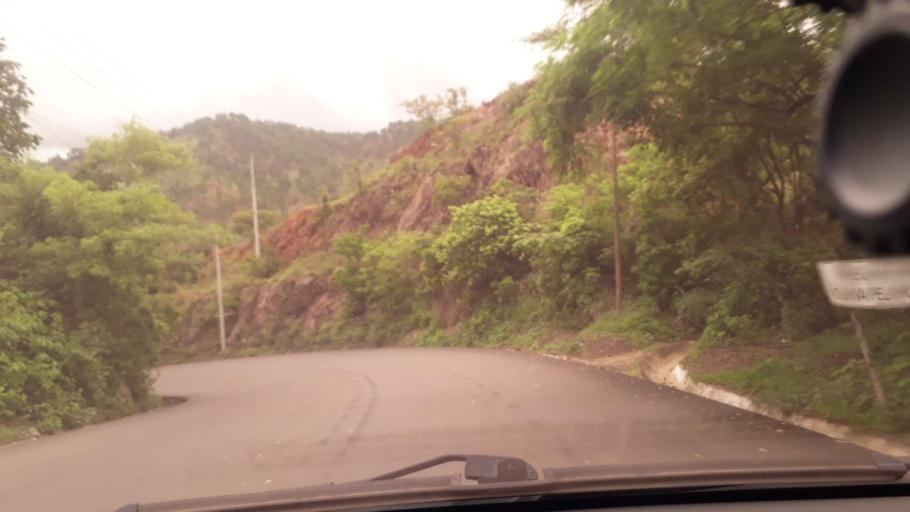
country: GT
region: Chiquimula
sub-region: Municipio de San Juan Ermita
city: San Juan Ermita
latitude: 14.7467
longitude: -89.4633
